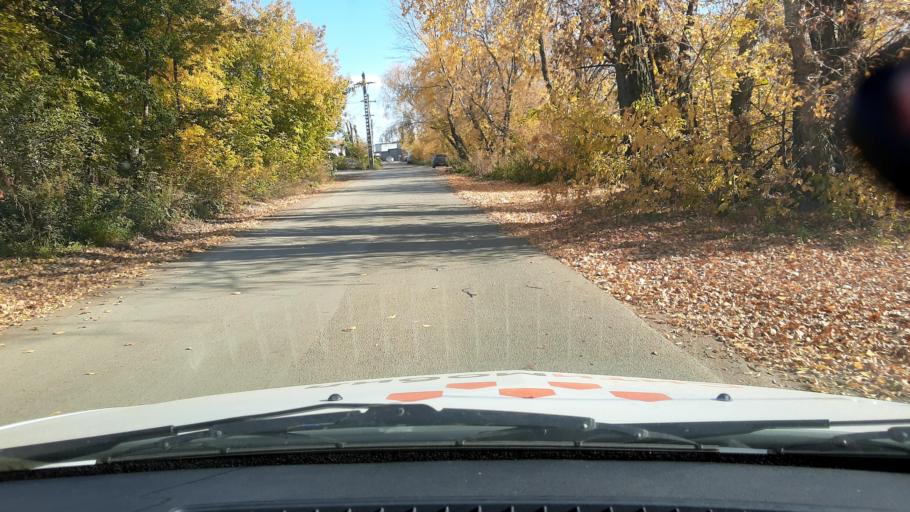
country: RU
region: Bashkortostan
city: Ufa
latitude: 54.7963
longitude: 56.0891
